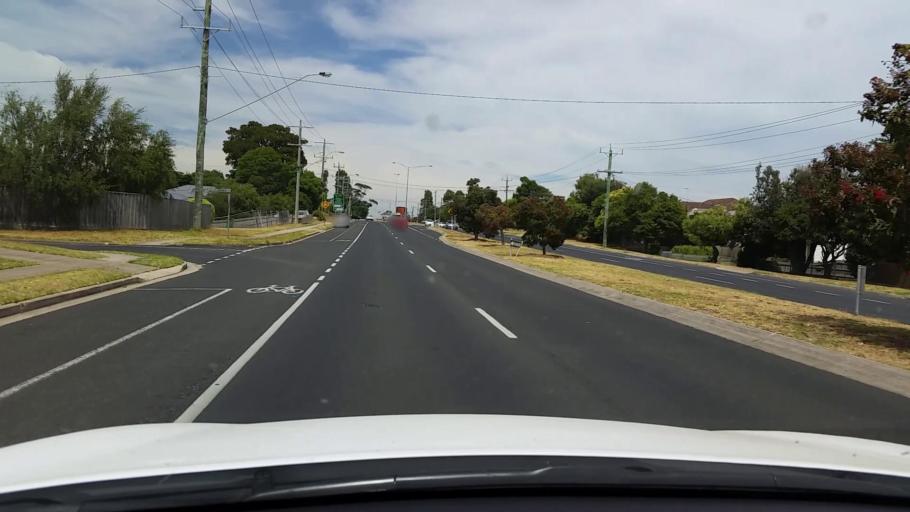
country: AU
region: Victoria
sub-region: Mornington Peninsula
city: Rosebud West
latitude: -38.3652
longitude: 144.8896
